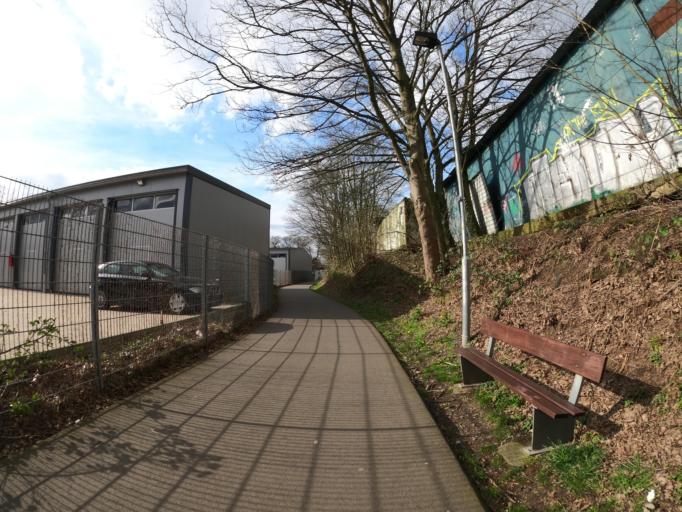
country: DE
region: North Rhine-Westphalia
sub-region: Regierungsbezirk Dusseldorf
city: Solingen
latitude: 51.1891
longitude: 7.0517
